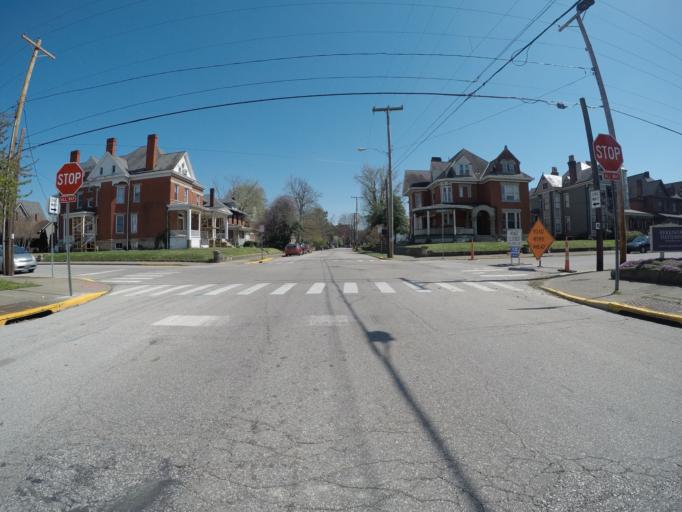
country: US
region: West Virginia
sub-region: Kanawha County
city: Charleston
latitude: 38.3428
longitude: -81.6277
